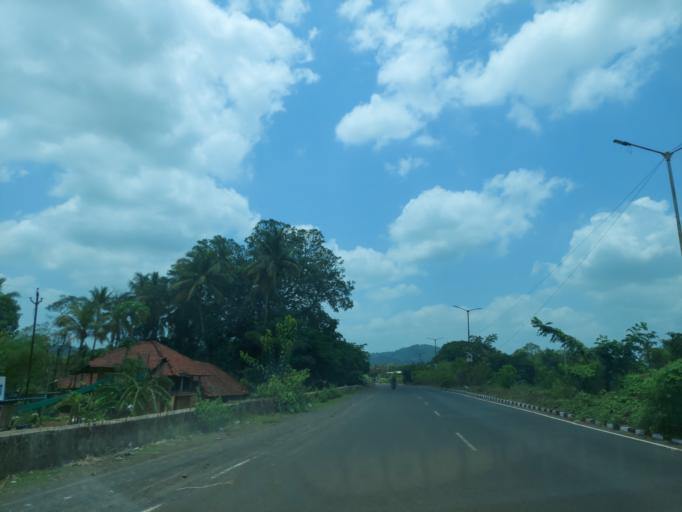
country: IN
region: Maharashtra
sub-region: Sindhudurg
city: Savantvadi
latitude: 15.8196
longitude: 73.8619
